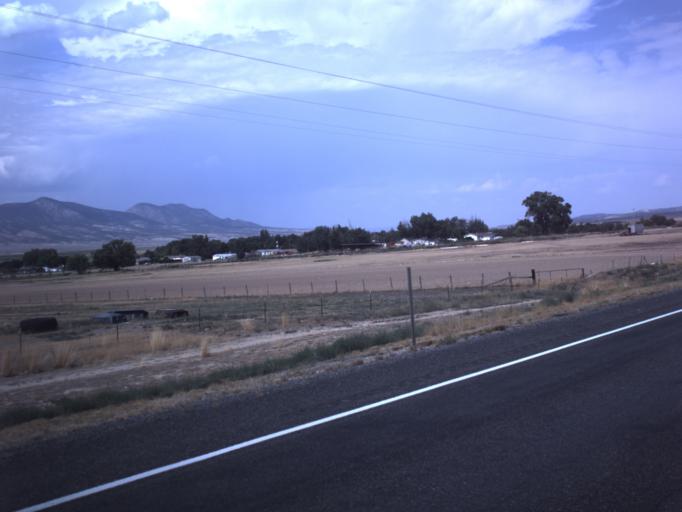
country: US
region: Utah
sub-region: Sanpete County
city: Gunnison
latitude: 39.2183
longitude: -111.8482
